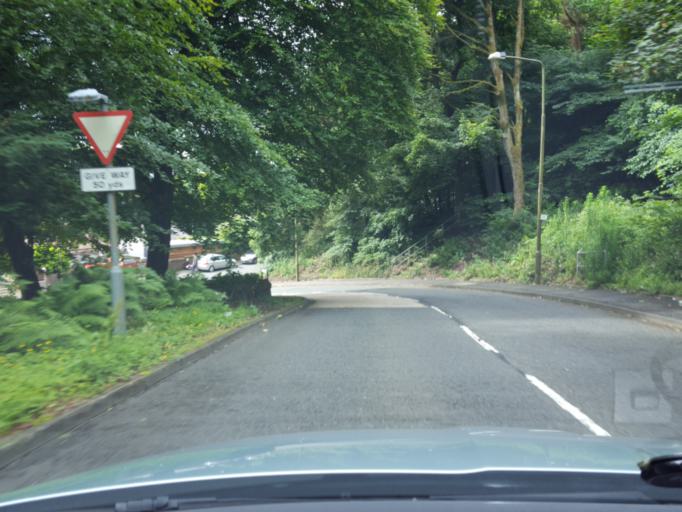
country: GB
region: Scotland
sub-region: West Lothian
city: Bathgate
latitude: 55.8969
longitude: -3.6197
